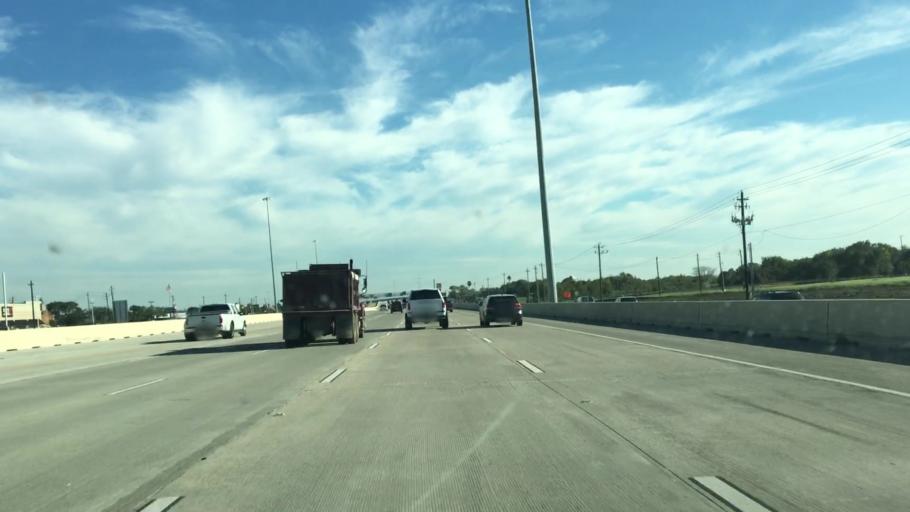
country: US
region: Texas
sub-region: Harris County
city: Webster
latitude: 29.5359
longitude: -95.1379
